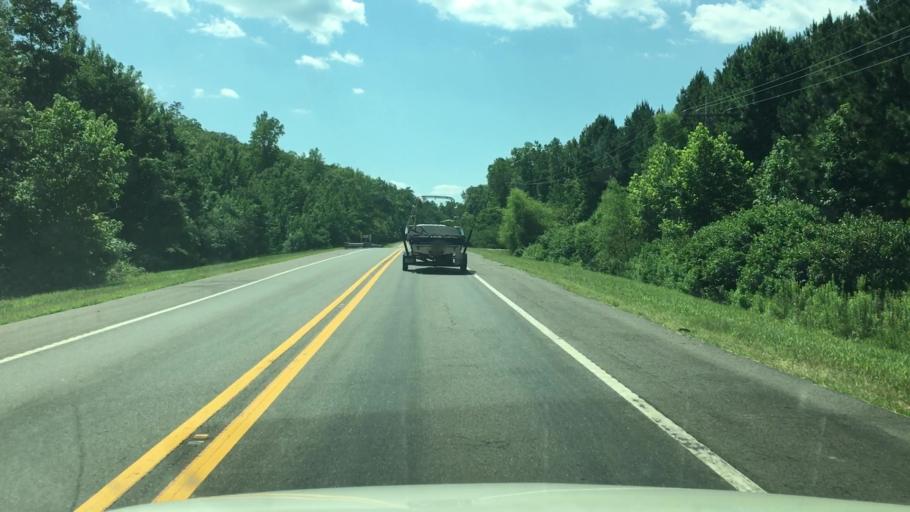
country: US
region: Arkansas
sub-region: Garland County
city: Rockwell
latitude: 34.5166
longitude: -93.2943
